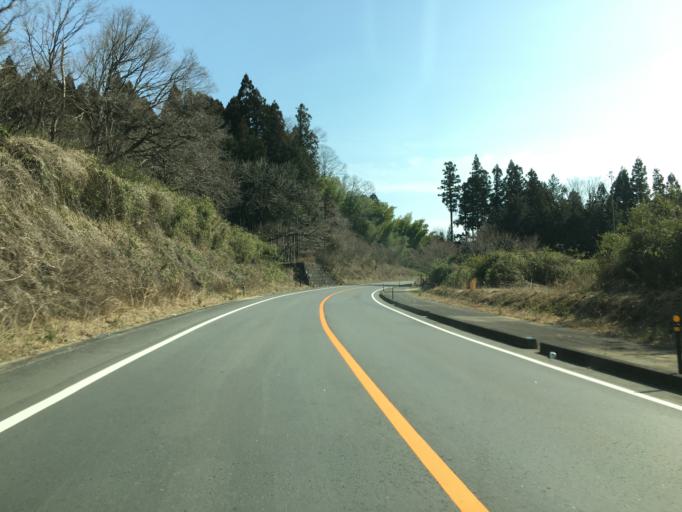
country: JP
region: Ibaraki
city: Daigo
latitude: 36.8090
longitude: 140.4691
